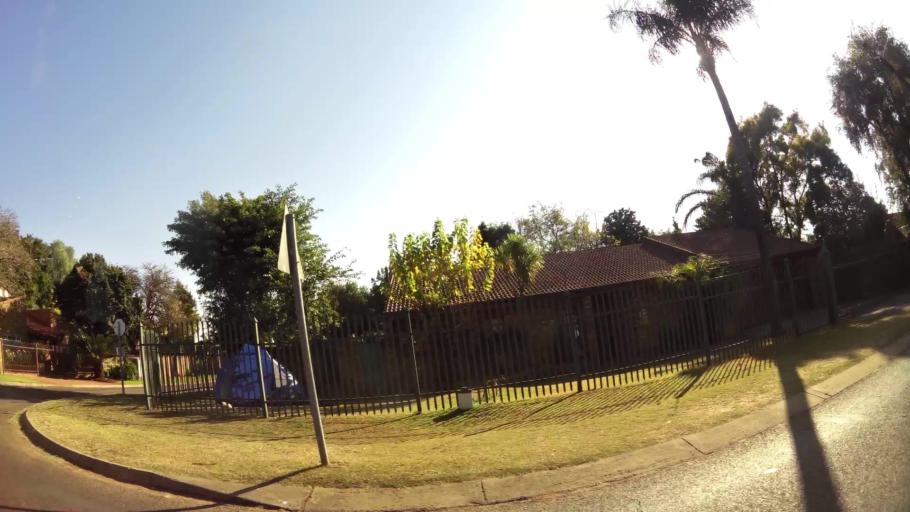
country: ZA
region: Gauteng
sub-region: City of Tshwane Metropolitan Municipality
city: Pretoria
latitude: -25.6669
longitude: 28.1436
